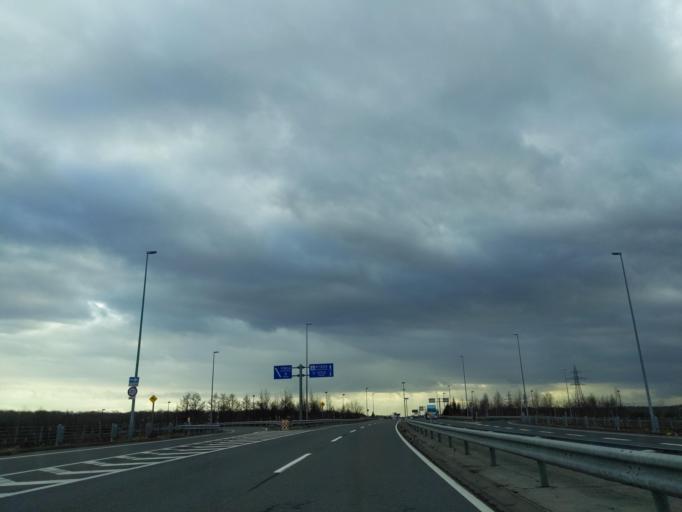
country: JP
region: Hokkaido
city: Chitose
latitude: 42.8279
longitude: 141.6894
